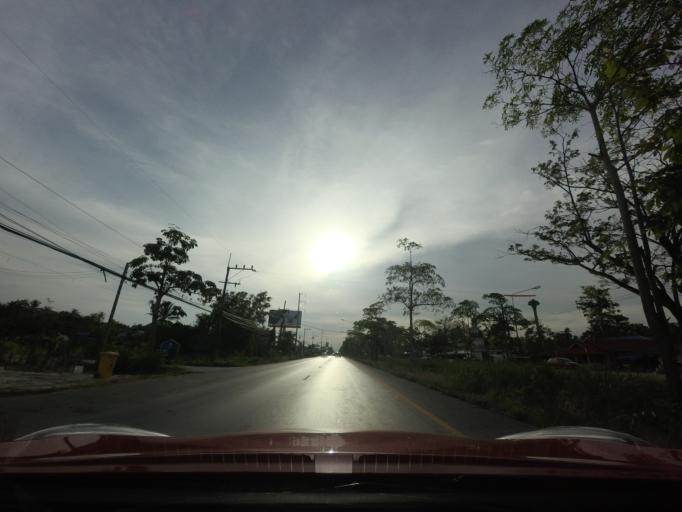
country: TH
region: Pattani
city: Nong Chik
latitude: 6.8039
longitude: 101.1383
